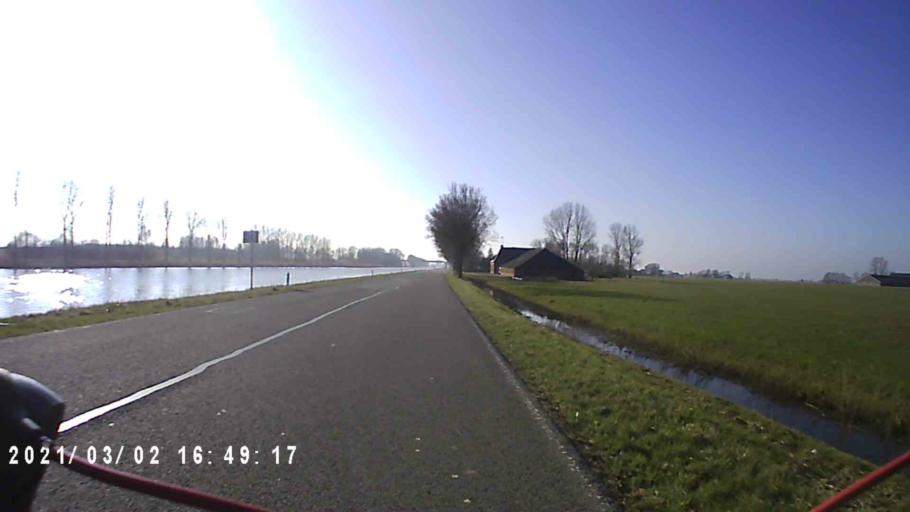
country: NL
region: Groningen
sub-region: Gemeente Grootegast
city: Grootegast
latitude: 53.2440
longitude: 6.2632
